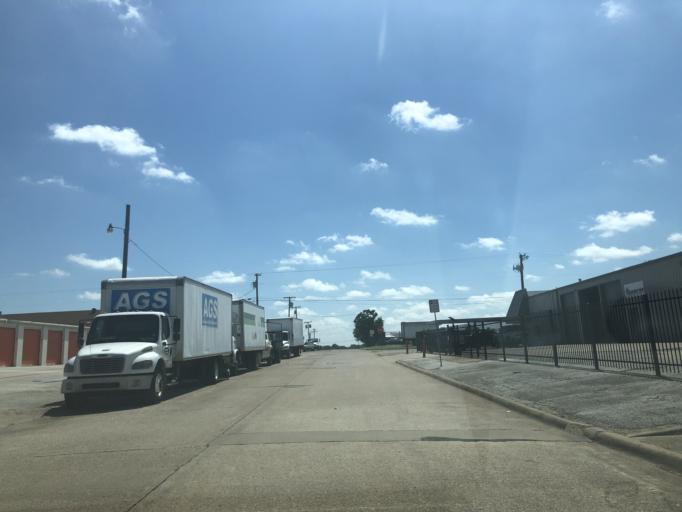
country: US
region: Texas
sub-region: Dallas County
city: Duncanville
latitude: 32.6450
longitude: -96.9233
